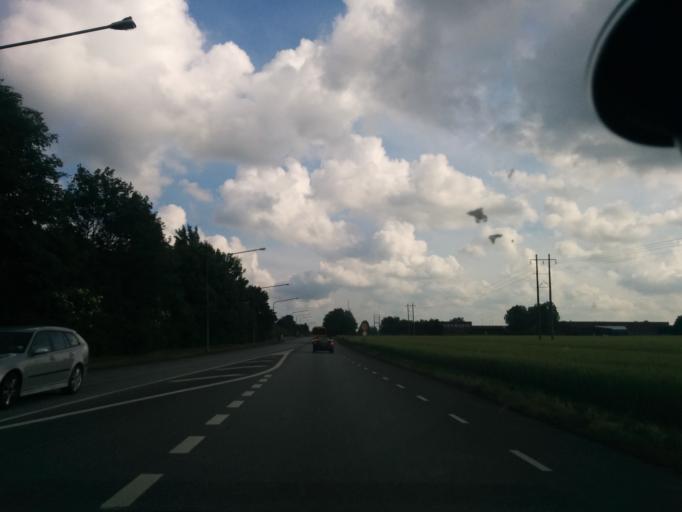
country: SE
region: Skane
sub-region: Staffanstorps Kommun
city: Staffanstorp
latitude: 55.6379
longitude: 13.1864
